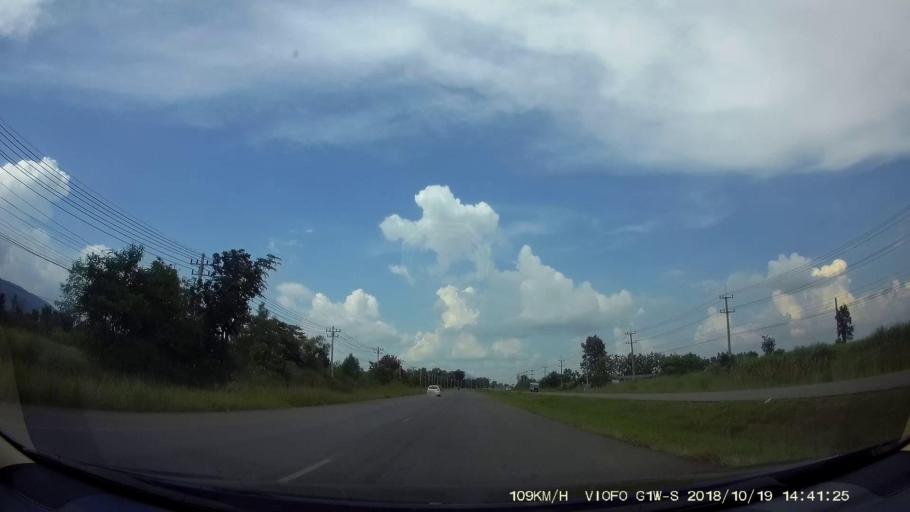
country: TH
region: Chaiyaphum
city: Phu Khiao
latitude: 16.2567
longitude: 102.1991
